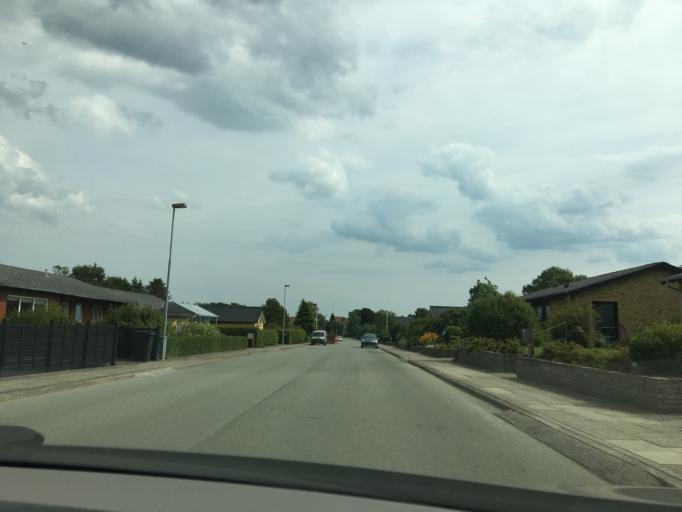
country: DK
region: Central Jutland
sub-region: Viborg Kommune
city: Stoholm
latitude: 56.4878
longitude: 9.1442
